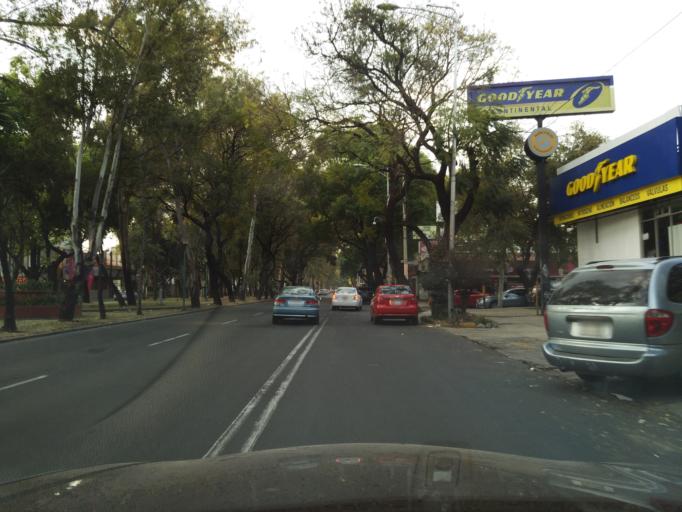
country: MX
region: Mexico City
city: Tlalpan
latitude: 19.3171
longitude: -99.1271
